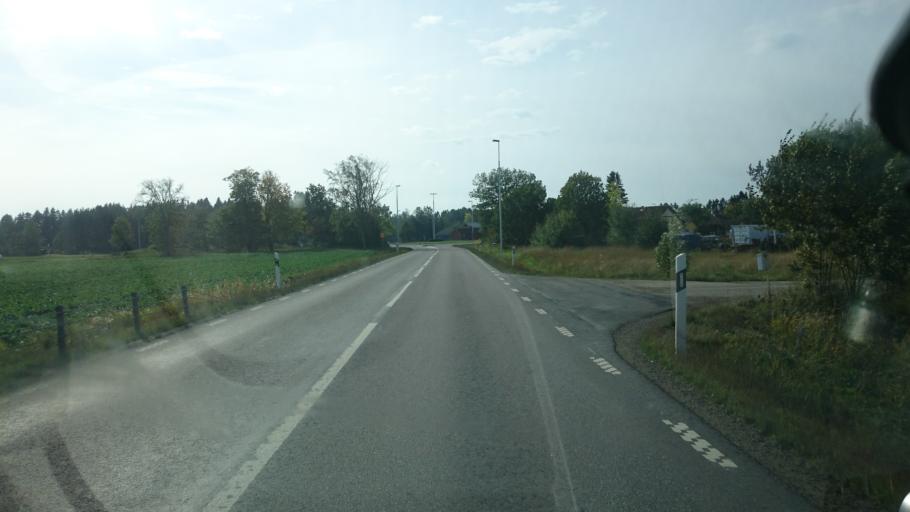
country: SE
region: Vaestra Goetaland
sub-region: Vanersborgs Kommun
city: Vargon
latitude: 58.2651
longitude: 12.4012
